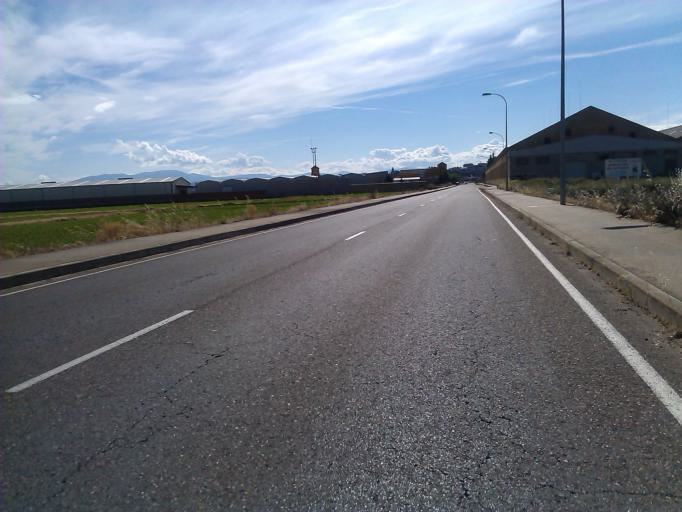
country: ES
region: Castille and Leon
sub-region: Provincia de Leon
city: San Justo de la Vega
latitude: 42.4542
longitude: -6.0312
